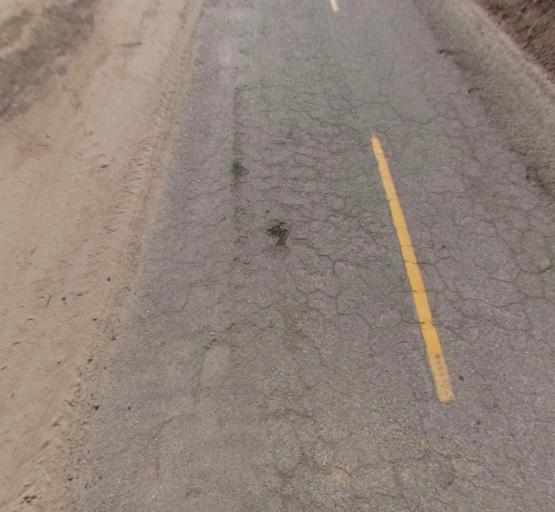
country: US
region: California
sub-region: Madera County
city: Madera
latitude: 36.9311
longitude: -120.1270
